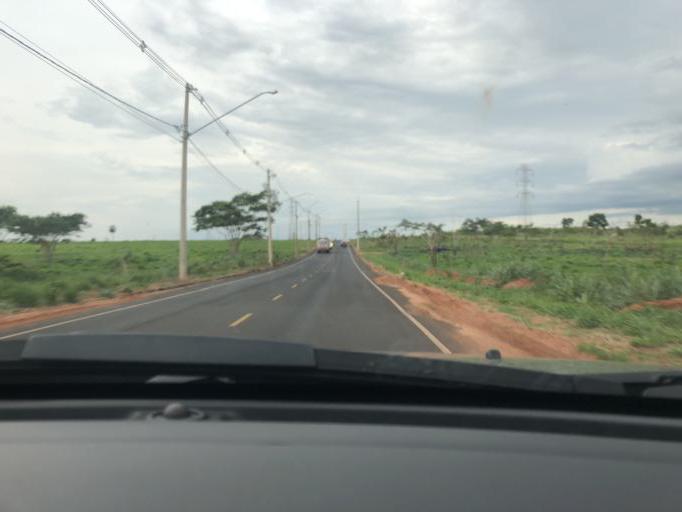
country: BR
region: Sao Paulo
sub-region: Sao Jose Do Rio Preto
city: Sao Jose do Rio Preto
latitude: -20.8324
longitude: -49.4253
